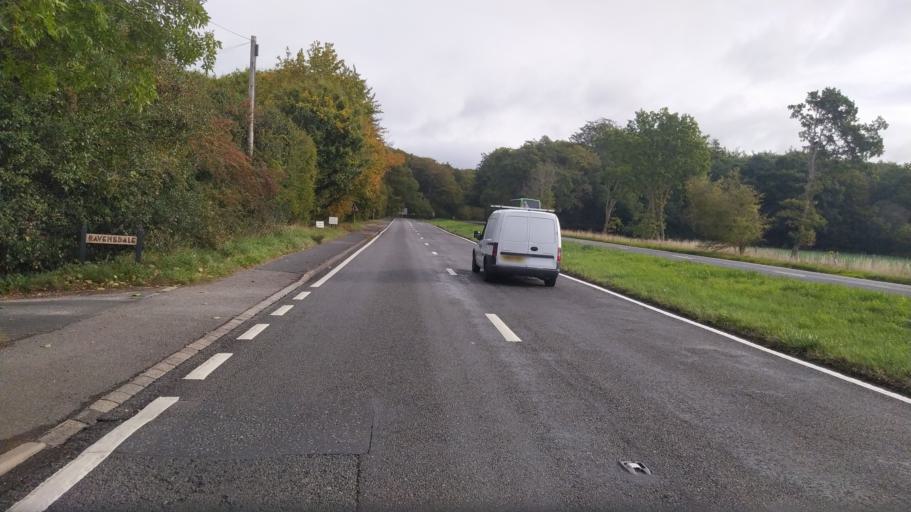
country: GB
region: England
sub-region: Hampshire
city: Eversley
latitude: 51.3162
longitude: -0.8866
